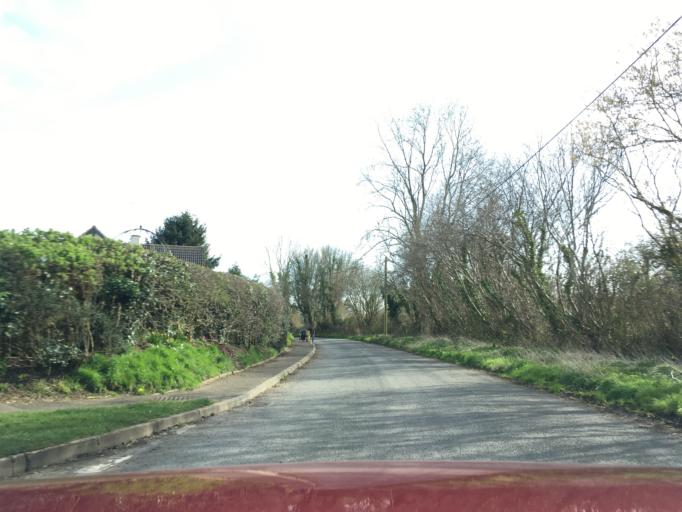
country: GB
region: England
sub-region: Wiltshire
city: Chippenham
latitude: 51.4941
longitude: -2.1118
